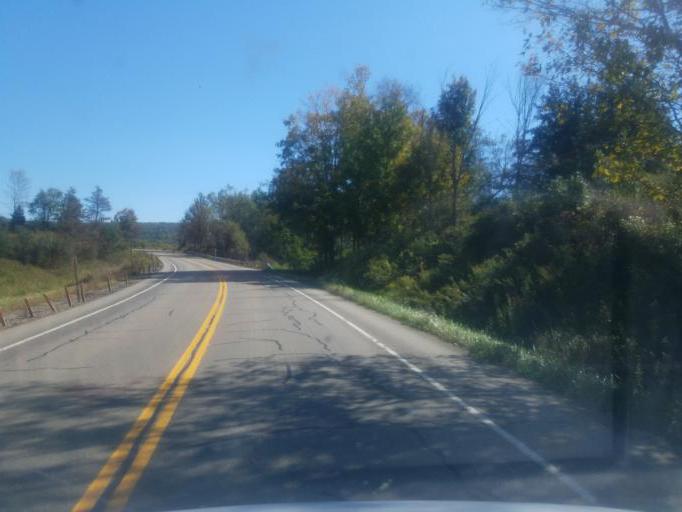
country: US
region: New York
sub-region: Allegany County
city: Friendship
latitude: 42.3010
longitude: -78.1613
